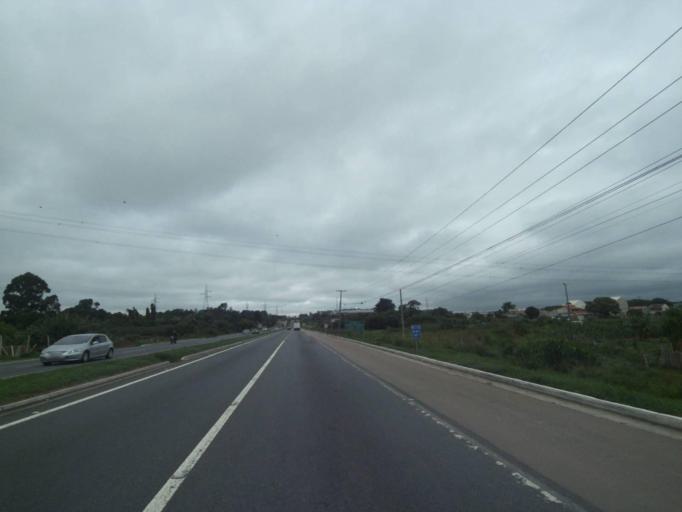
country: BR
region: Parana
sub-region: Araucaria
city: Araucaria
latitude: -25.5549
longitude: -49.3401
